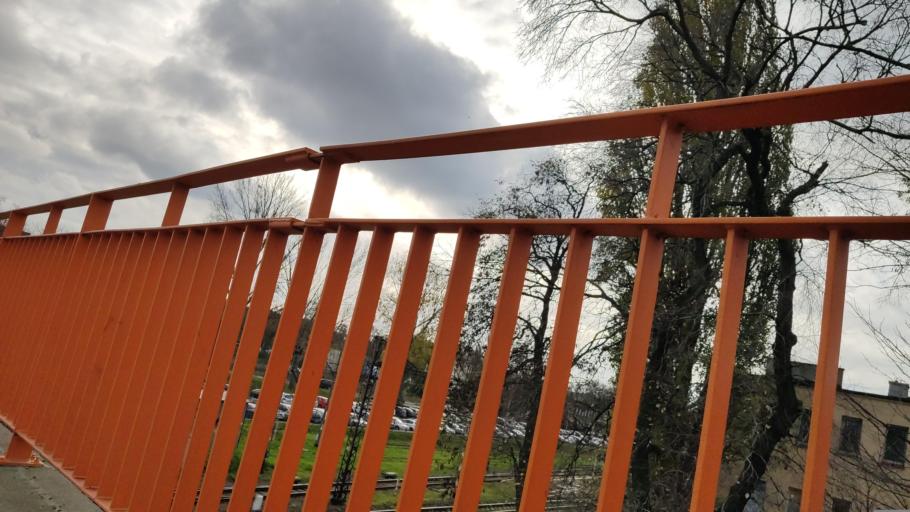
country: PL
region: Kujawsko-Pomorskie
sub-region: Powiat inowroclawski
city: Inowroclaw
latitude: 52.8068
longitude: 18.2457
